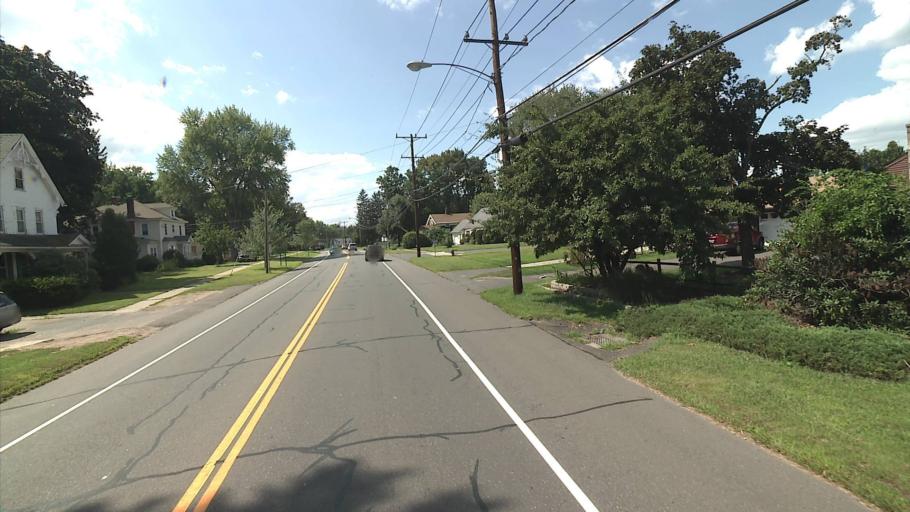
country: US
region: Connecticut
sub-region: Hartford County
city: Hazardville
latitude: 41.9853
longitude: -72.5242
